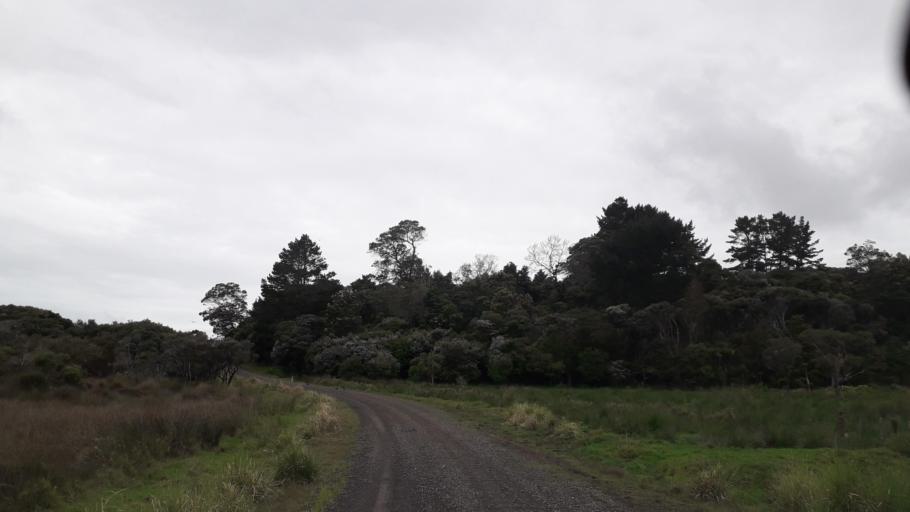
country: NZ
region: Northland
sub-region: Far North District
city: Kaitaia
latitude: -35.3934
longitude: 173.4050
